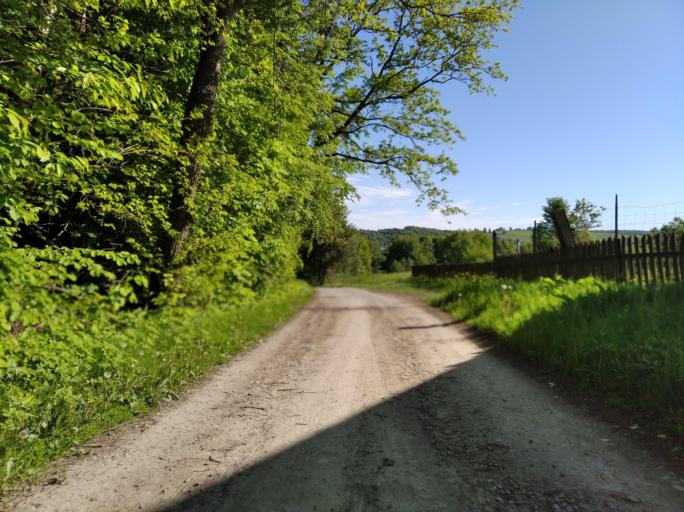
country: PL
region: Subcarpathian Voivodeship
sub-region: Powiat strzyzowski
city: Frysztak
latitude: 49.8405
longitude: 21.5608
